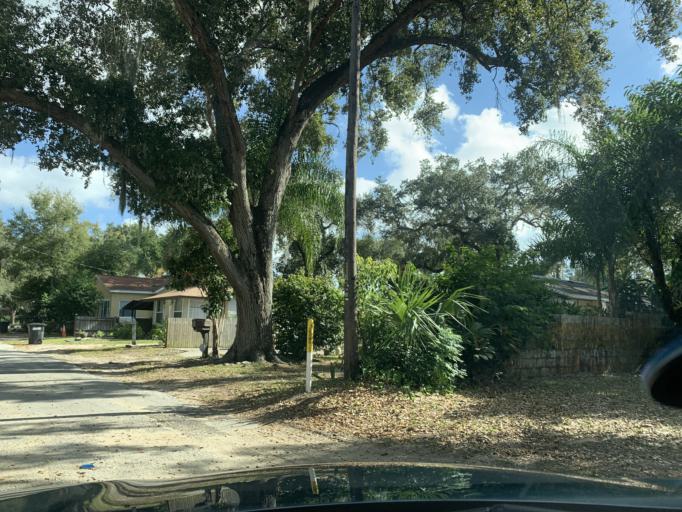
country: US
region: Florida
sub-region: Pinellas County
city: Belleair
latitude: 27.9397
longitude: -82.7967
